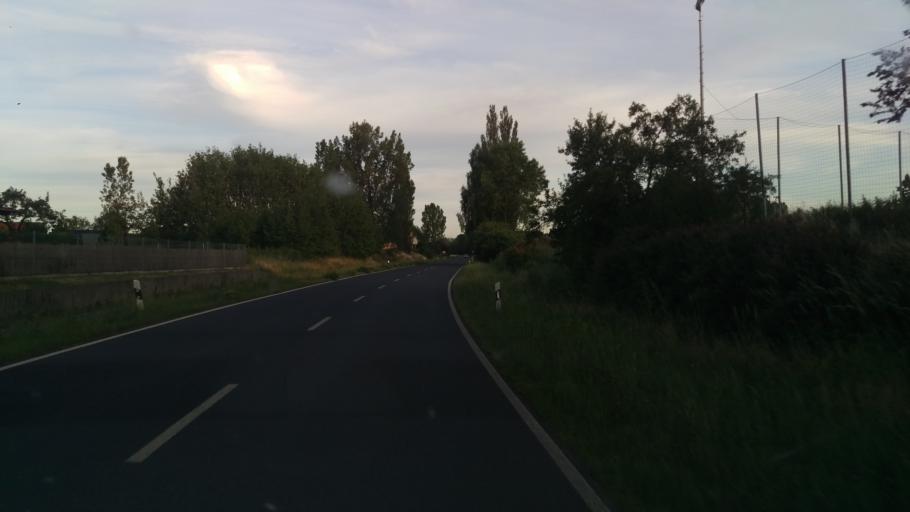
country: DE
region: Brandenburg
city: Vogelsang
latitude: 52.1804
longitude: 14.6653
